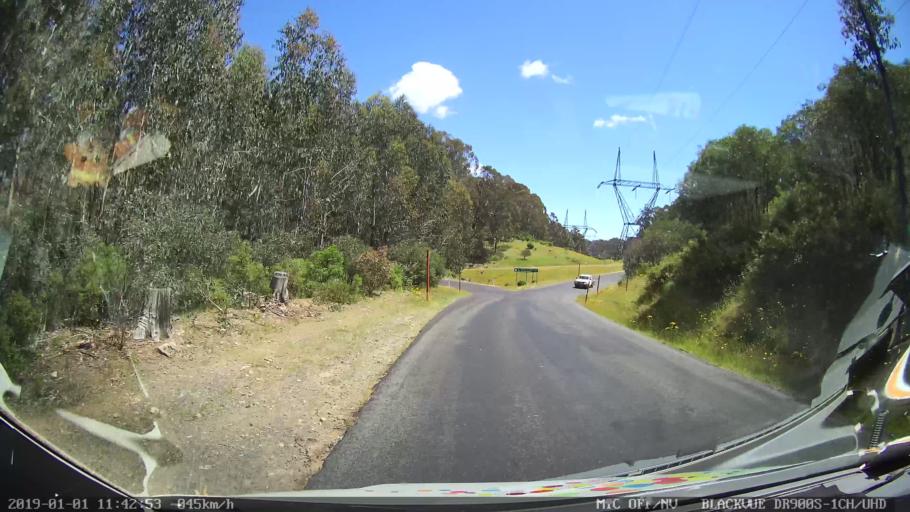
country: AU
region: New South Wales
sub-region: Snowy River
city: Jindabyne
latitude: -35.9064
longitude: 148.3836
